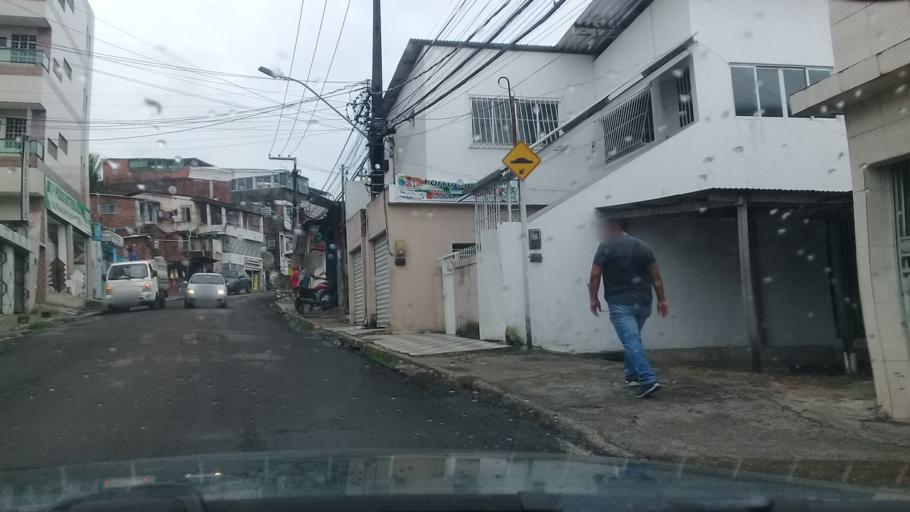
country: BR
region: Pernambuco
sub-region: Jaboatao Dos Guararapes
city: Jaboatao dos Guararapes
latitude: -8.0878
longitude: -34.9742
